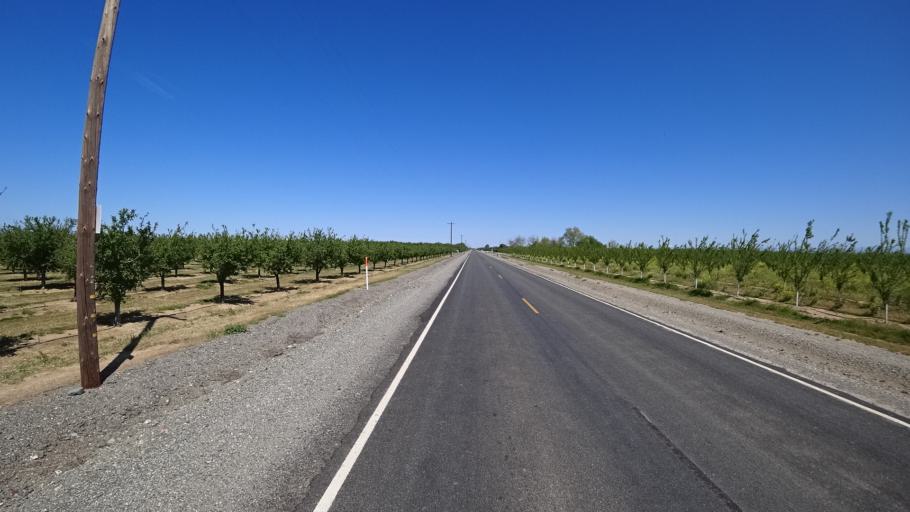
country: US
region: California
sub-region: Glenn County
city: Orland
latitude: 39.6687
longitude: -122.1406
